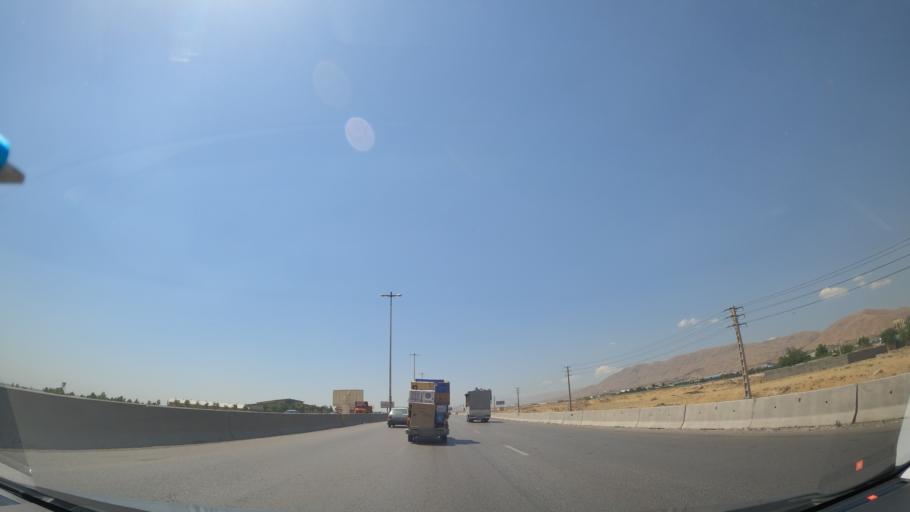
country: IR
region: Alborz
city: Karaj
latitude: 35.8740
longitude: 50.8936
